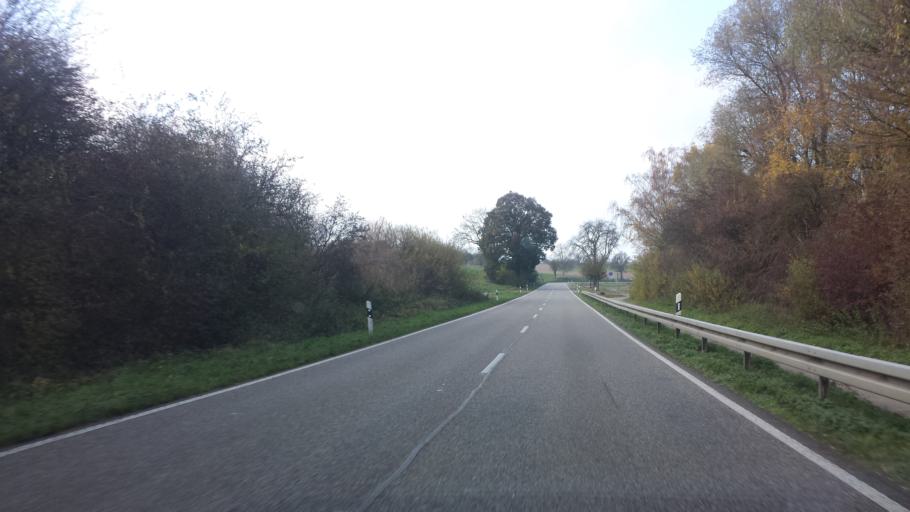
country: DE
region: Baden-Wuerttemberg
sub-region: Karlsruhe Region
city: Ubstadt-Weiher
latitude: 49.1301
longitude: 8.6961
